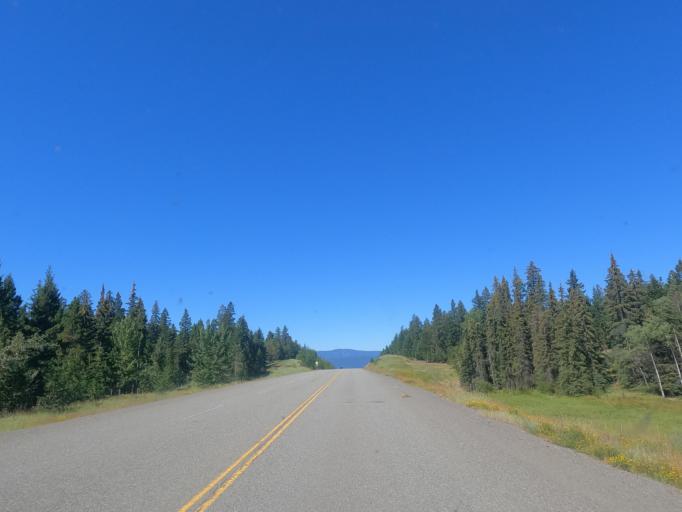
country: CA
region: British Columbia
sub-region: Thompson-Nicola Regional District
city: Ashcroft
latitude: 50.5707
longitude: -121.1999
